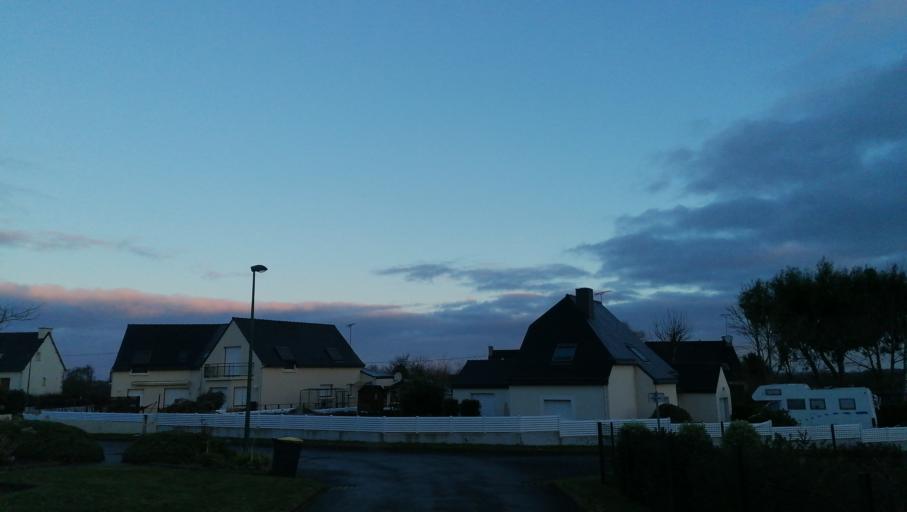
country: FR
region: Brittany
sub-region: Departement des Cotes-d'Armor
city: Plelo
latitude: 48.5529
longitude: -2.9512
